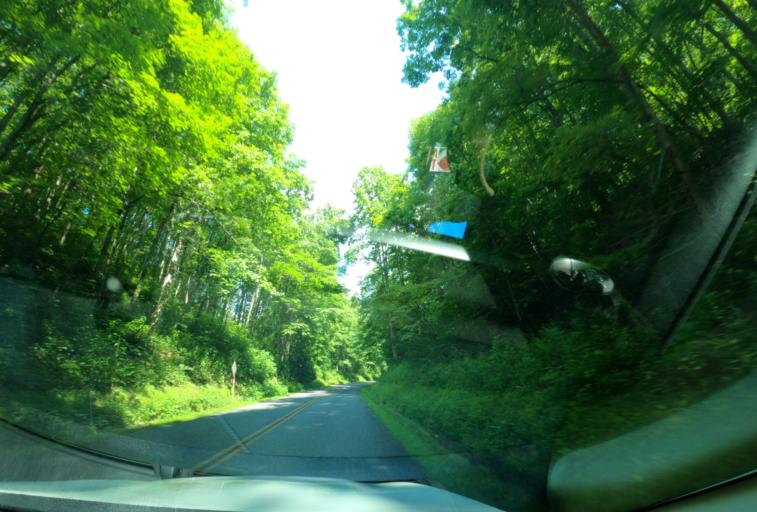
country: US
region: North Carolina
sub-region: Haywood County
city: Hazelwood
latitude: 35.4352
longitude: -83.0792
